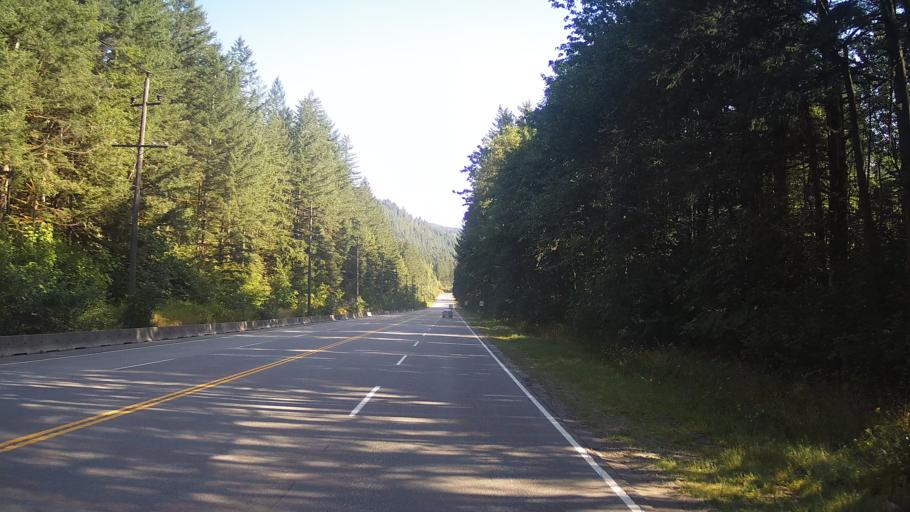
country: CA
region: British Columbia
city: Hope
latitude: 49.4522
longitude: -121.4370
